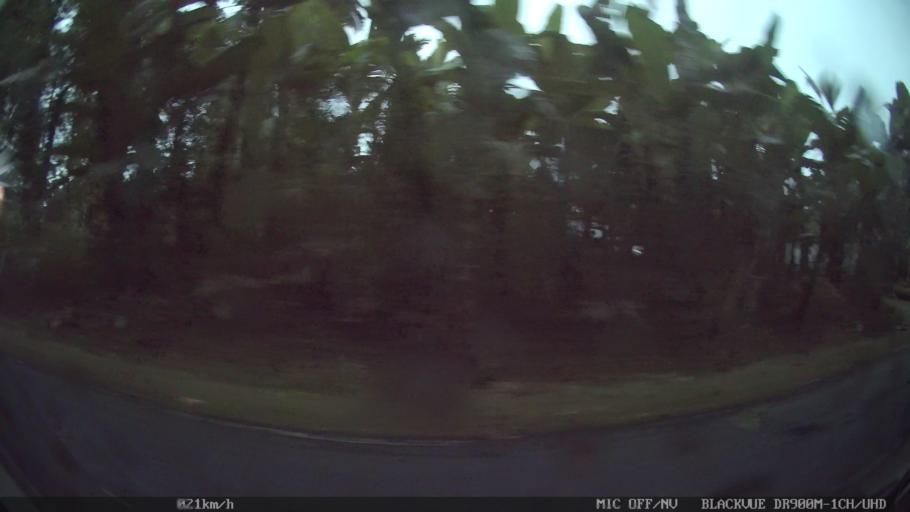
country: ID
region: Bali
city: Banjar Ponggang
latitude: -8.3854
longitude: 115.2625
